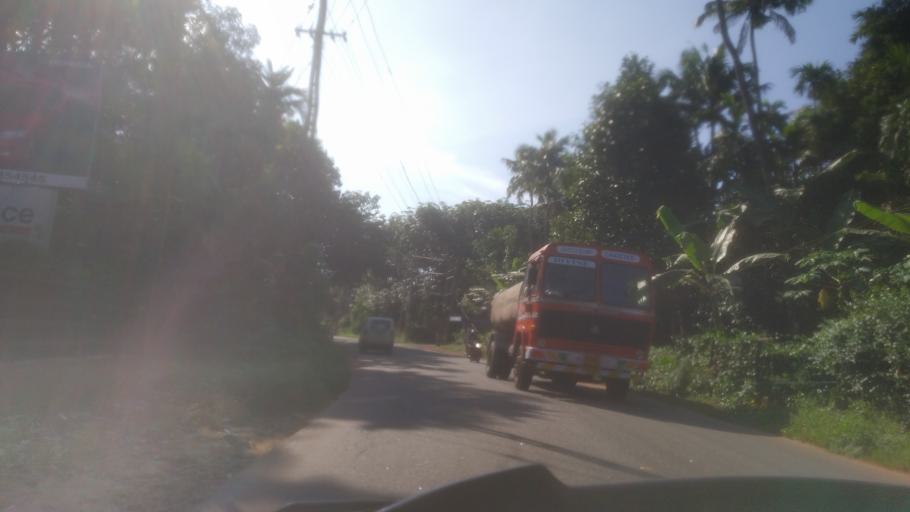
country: IN
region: Kerala
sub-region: Ernakulam
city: Muvattupuzha
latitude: 9.9807
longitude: 76.5463
